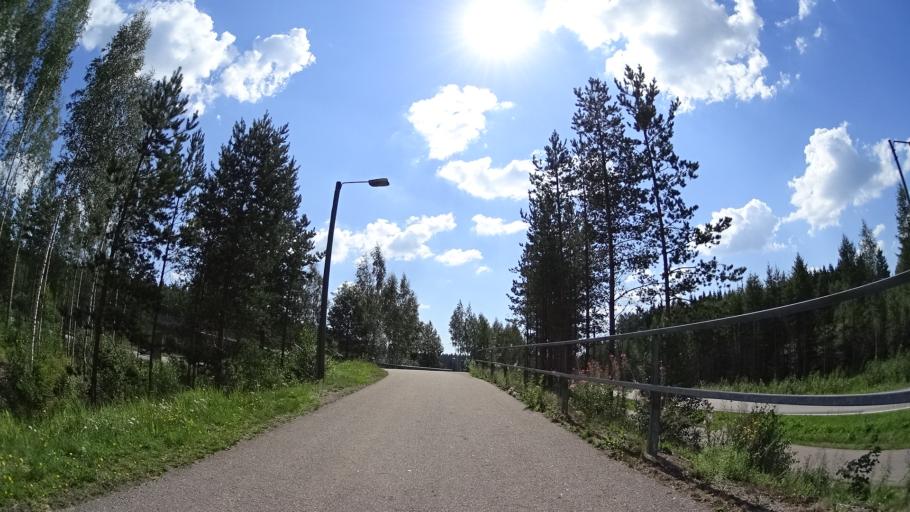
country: FI
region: Uusimaa
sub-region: Helsinki
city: Tuusula
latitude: 60.3584
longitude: 24.9993
